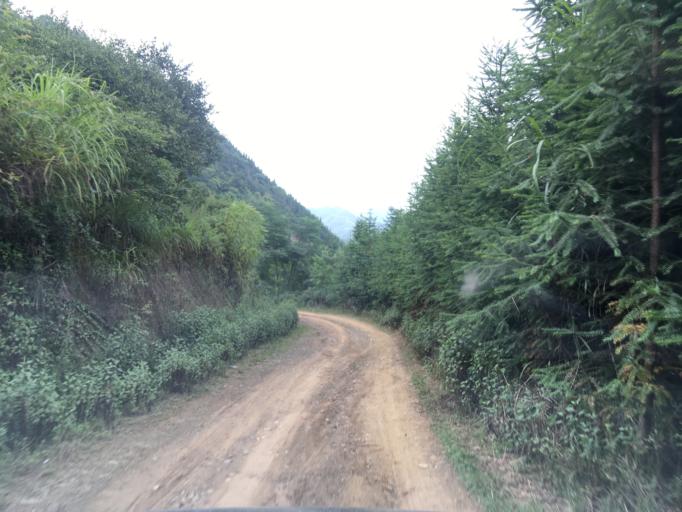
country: CN
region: Guangxi Zhuangzu Zizhiqu
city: Xinzhou
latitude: 24.8743
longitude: 105.8454
